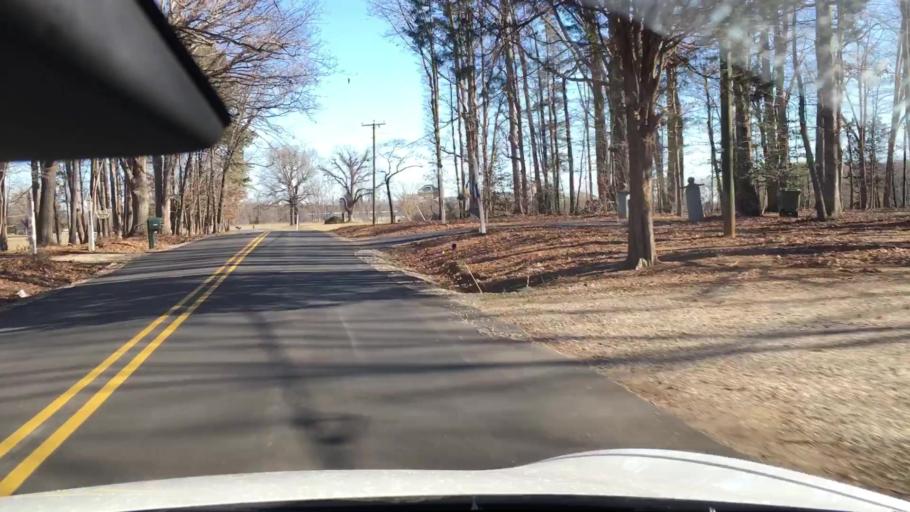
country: US
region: Virginia
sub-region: Powhatan County
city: Powhatan
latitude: 37.5648
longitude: -77.7879
